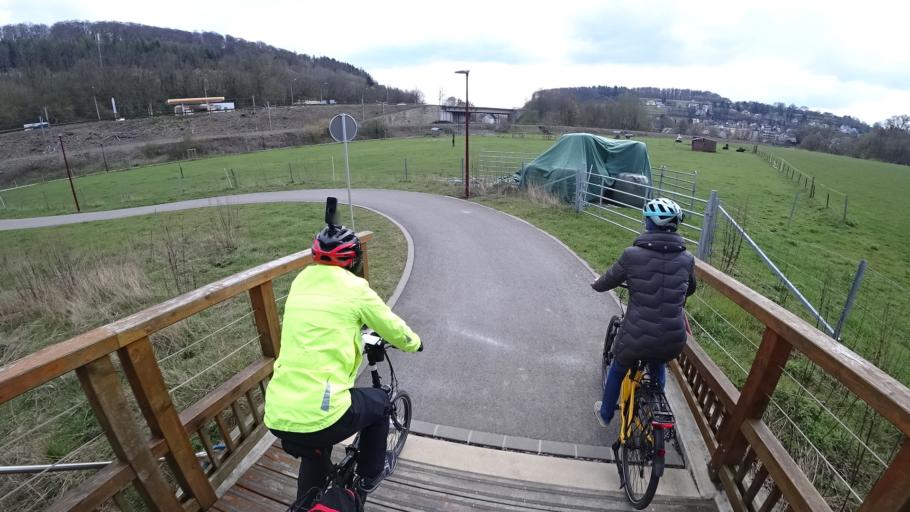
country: LU
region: Luxembourg
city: Colmar
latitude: 49.8176
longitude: 6.0958
